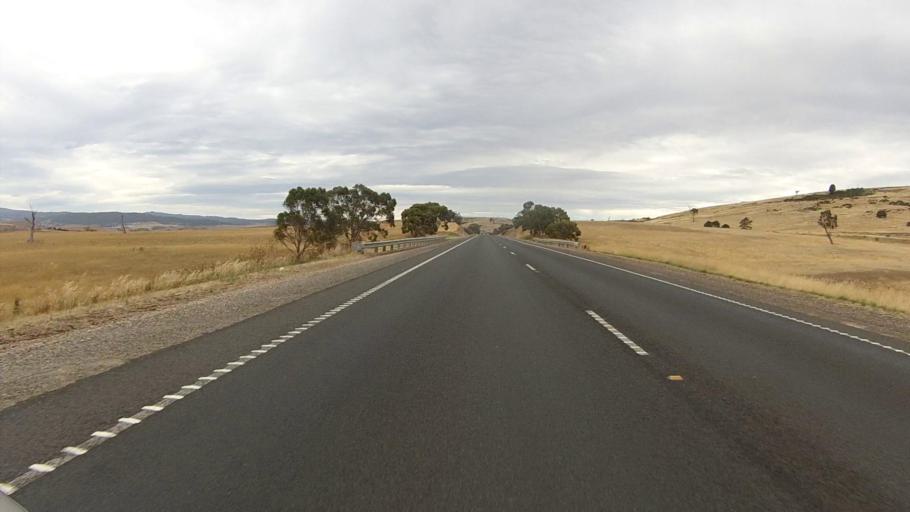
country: AU
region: Tasmania
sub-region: Brighton
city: Bridgewater
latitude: -42.3550
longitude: 147.3368
